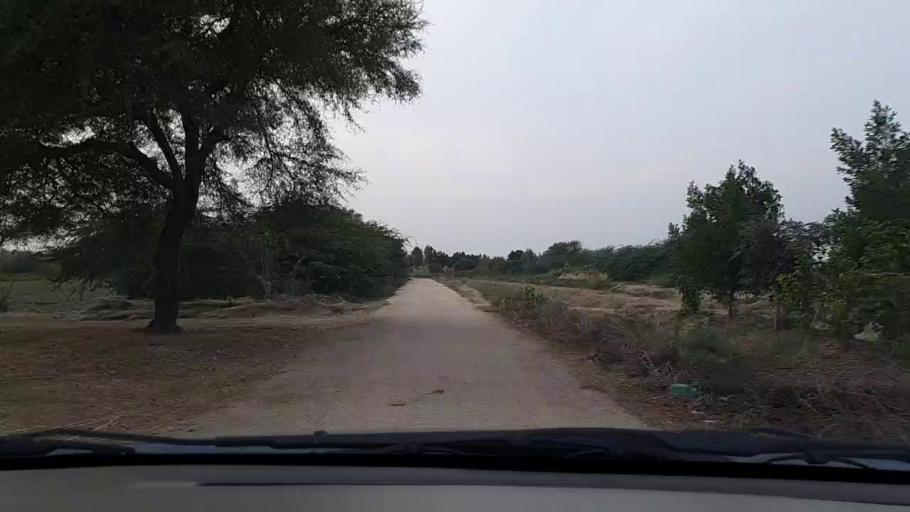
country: PK
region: Sindh
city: Thatta
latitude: 24.7699
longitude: 67.9243
